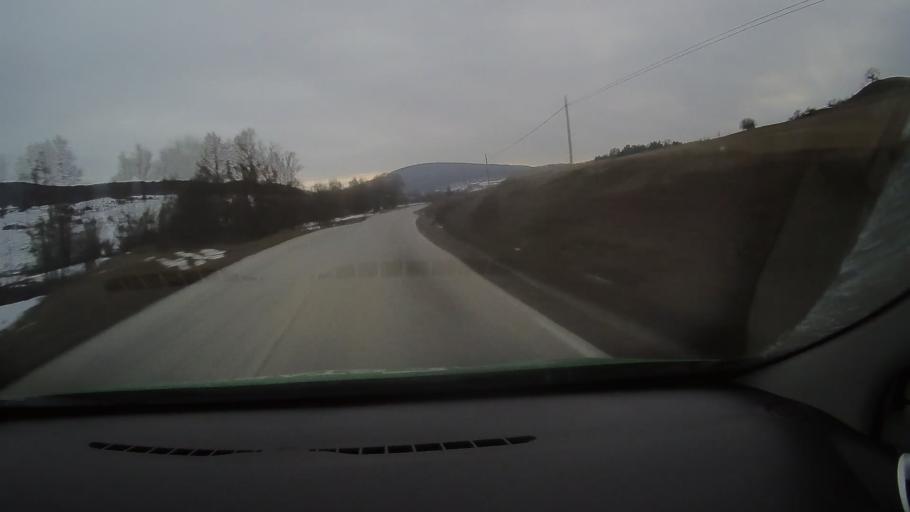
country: RO
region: Harghita
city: Taureni
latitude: 46.2371
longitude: 25.2497
